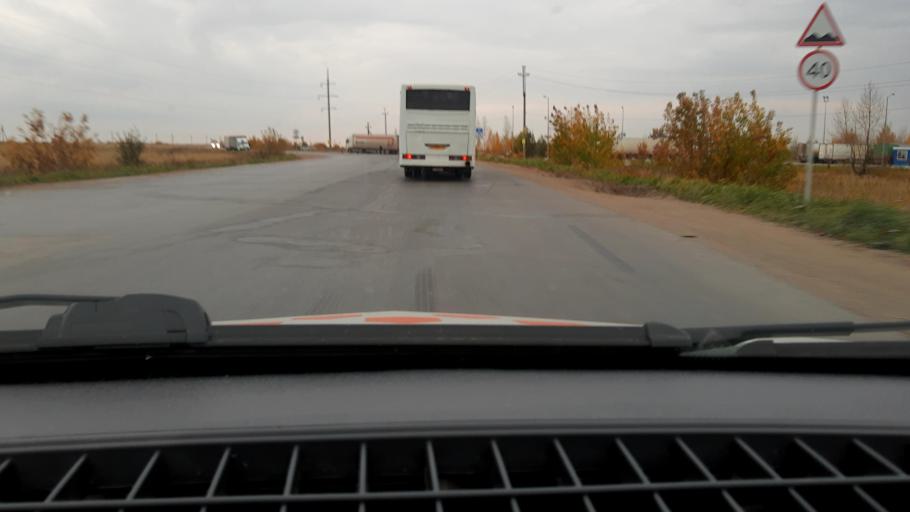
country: RU
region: Bashkortostan
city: Iglino
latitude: 54.7659
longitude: 56.2627
